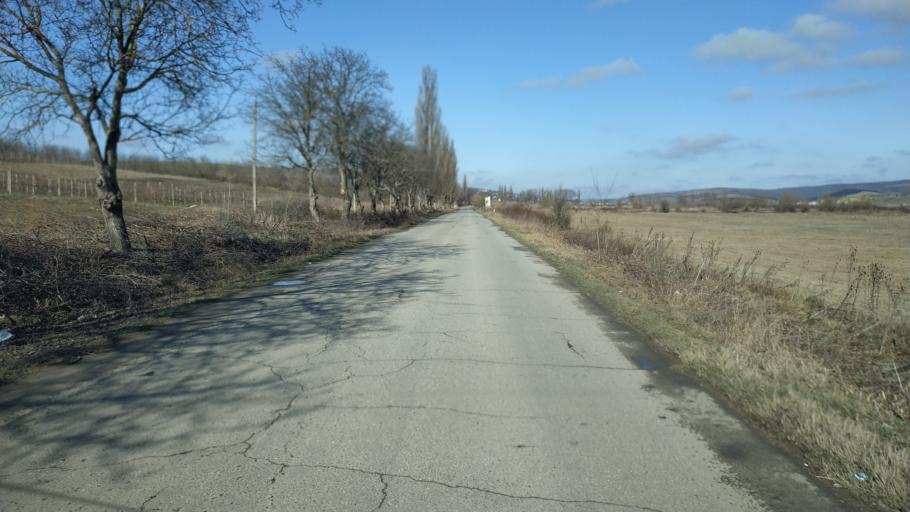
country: MD
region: Hincesti
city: Hincesti
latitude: 46.9448
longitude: 28.6227
